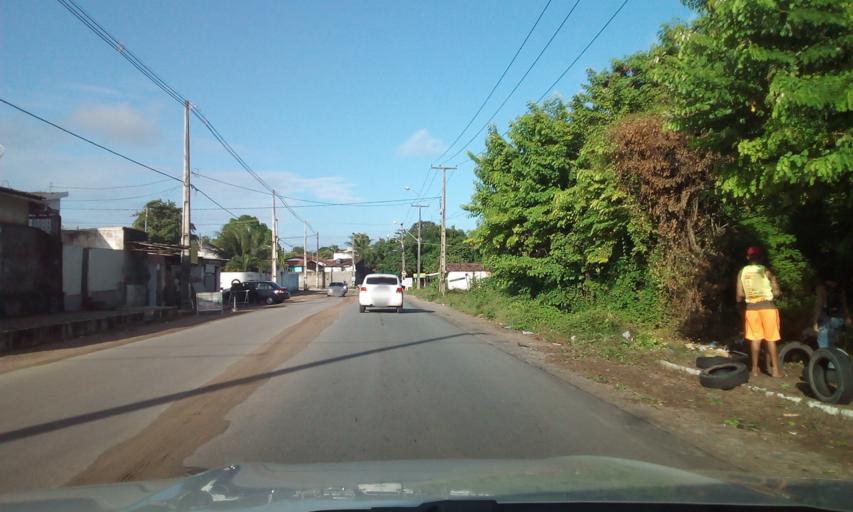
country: BR
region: Paraiba
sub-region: Joao Pessoa
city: Joao Pessoa
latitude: -7.1711
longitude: -34.8325
